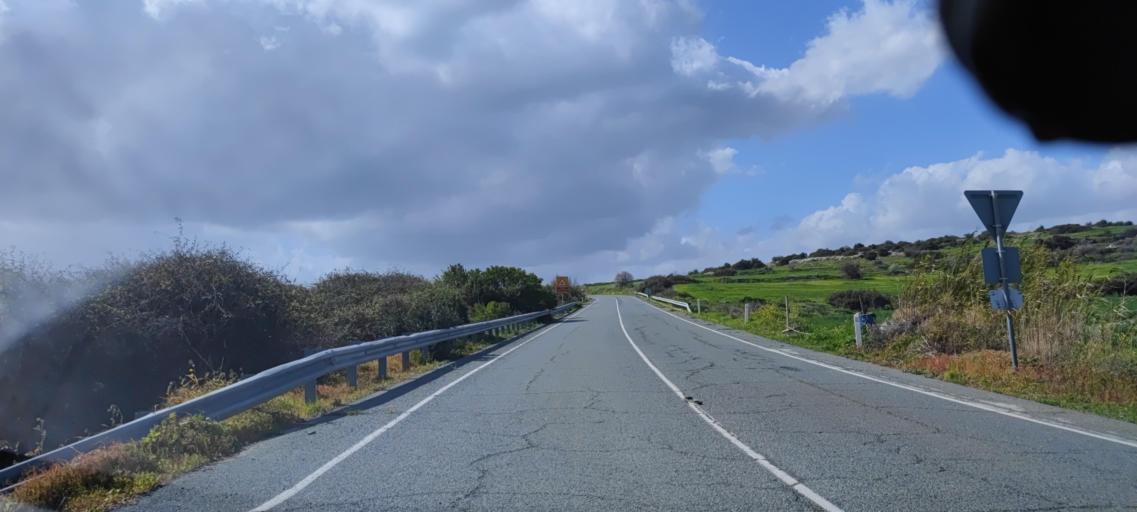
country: CY
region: Limassol
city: Pissouri
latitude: 34.6779
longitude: 32.7589
